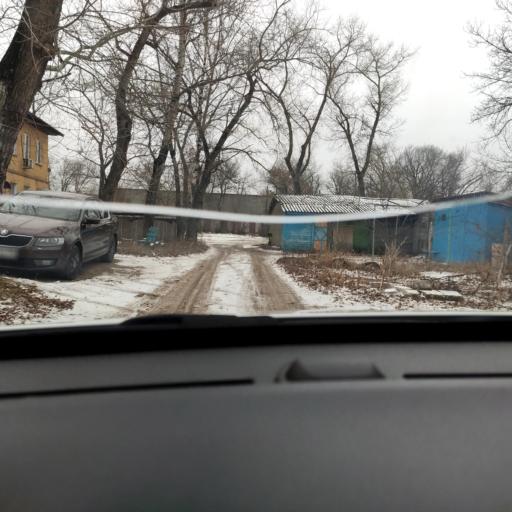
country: RU
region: Voronezj
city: Somovo
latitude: 51.7141
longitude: 39.2761
